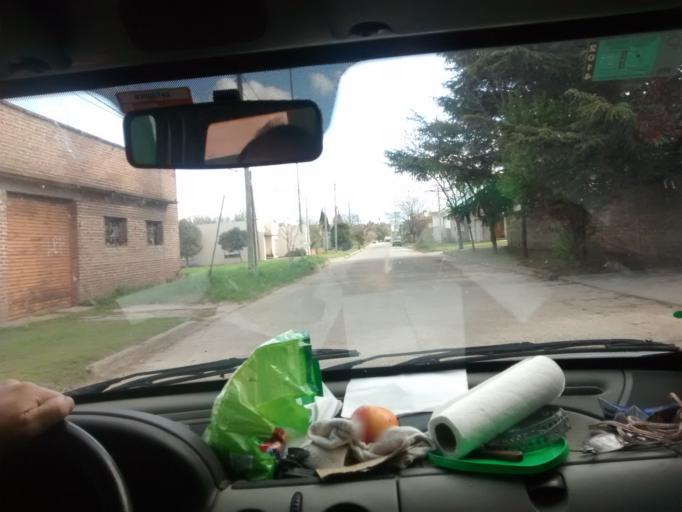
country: AR
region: Buenos Aires
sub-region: Partido de Loberia
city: Loberia
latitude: -38.1707
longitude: -58.7752
